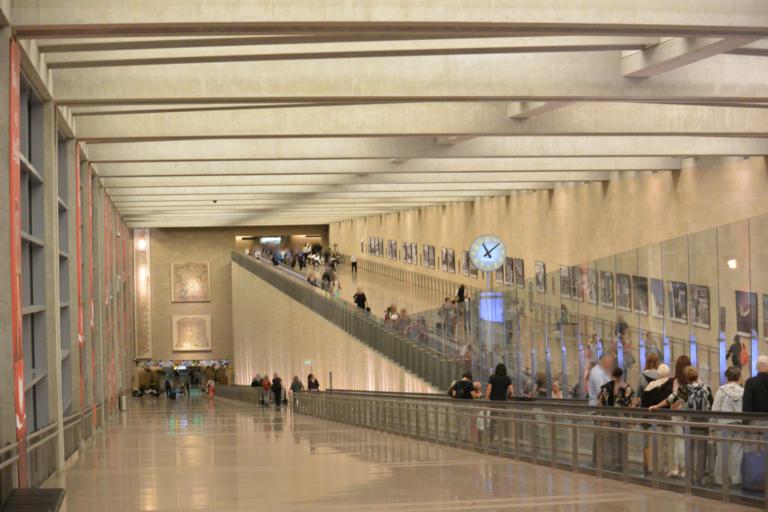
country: IL
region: Central District
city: Kefar Habad
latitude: 32.0030
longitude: 34.8725
